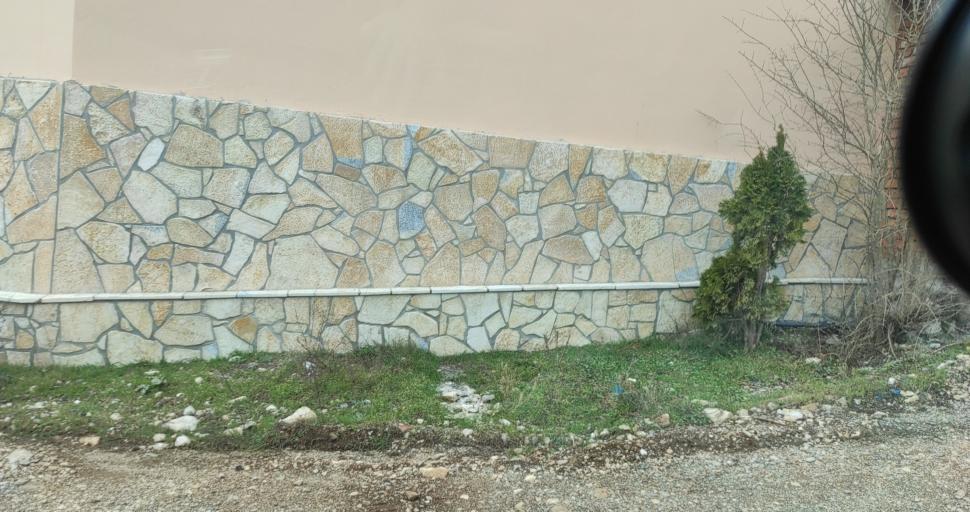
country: AL
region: Lezhe
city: Shengjin
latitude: 41.8135
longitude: 19.5823
